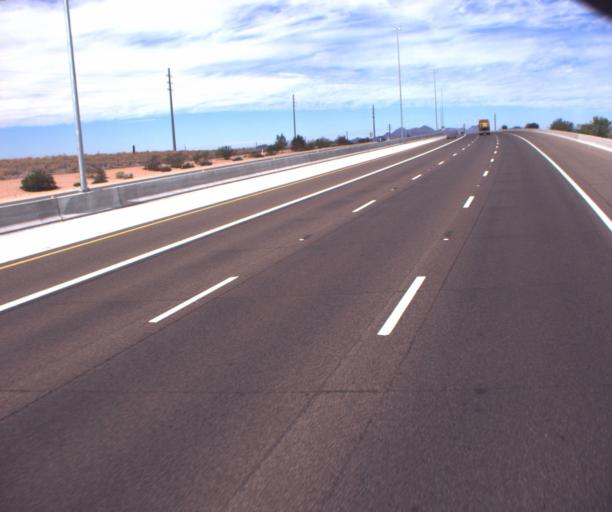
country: US
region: Arizona
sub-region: Pinal County
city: Apache Junction
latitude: 33.4667
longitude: -111.6795
